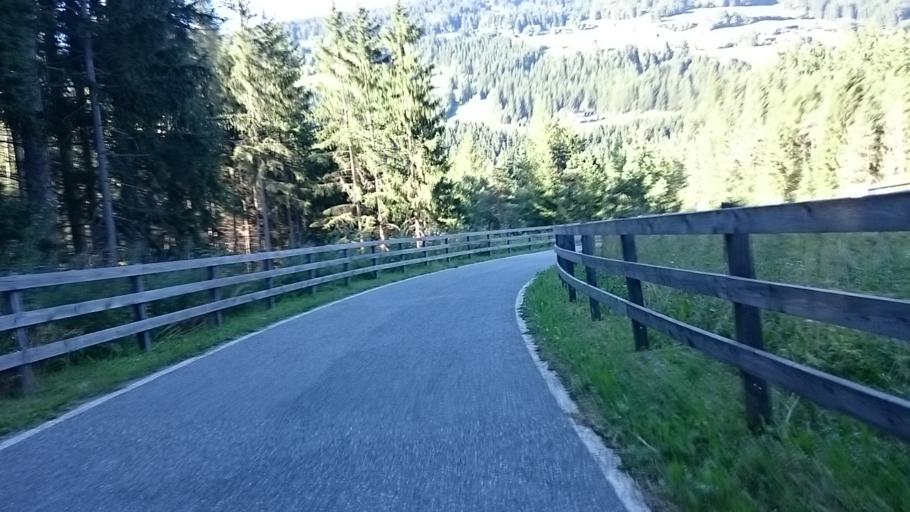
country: IT
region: Trentino-Alto Adige
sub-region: Bolzano
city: Braies
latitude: 46.7387
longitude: 12.1336
